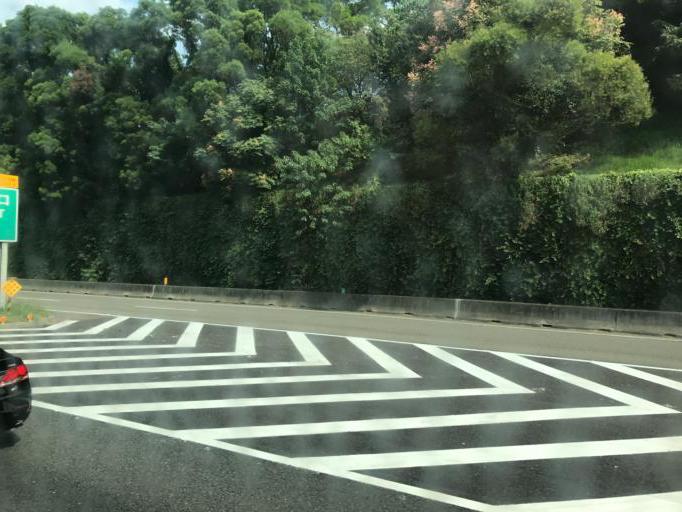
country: TW
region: Taiwan
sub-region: Hsinchu
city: Hsinchu
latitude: 24.7710
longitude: 121.0033
